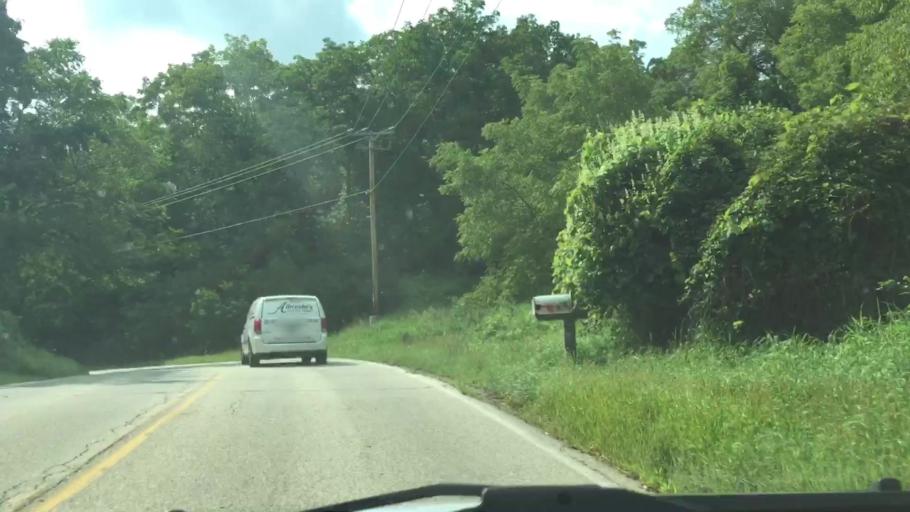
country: US
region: Wisconsin
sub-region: Waukesha County
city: Wales
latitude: 43.0408
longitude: -88.3509
